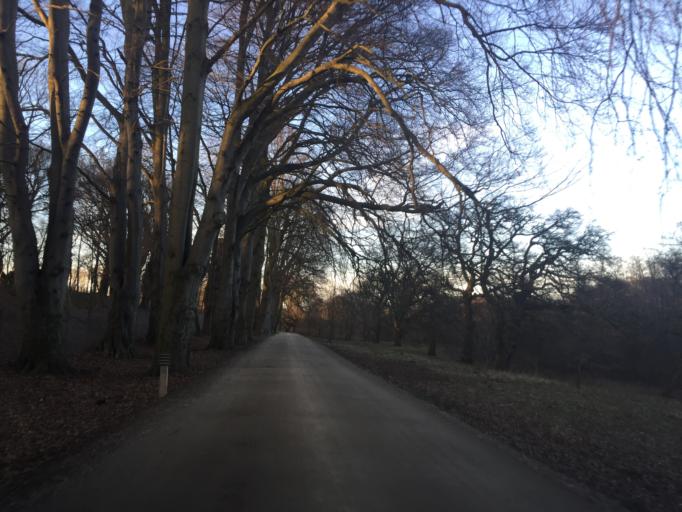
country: DK
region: Capital Region
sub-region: Lyngby-Tarbaek Kommune
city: Kongens Lyngby
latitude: 55.7879
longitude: 12.4976
